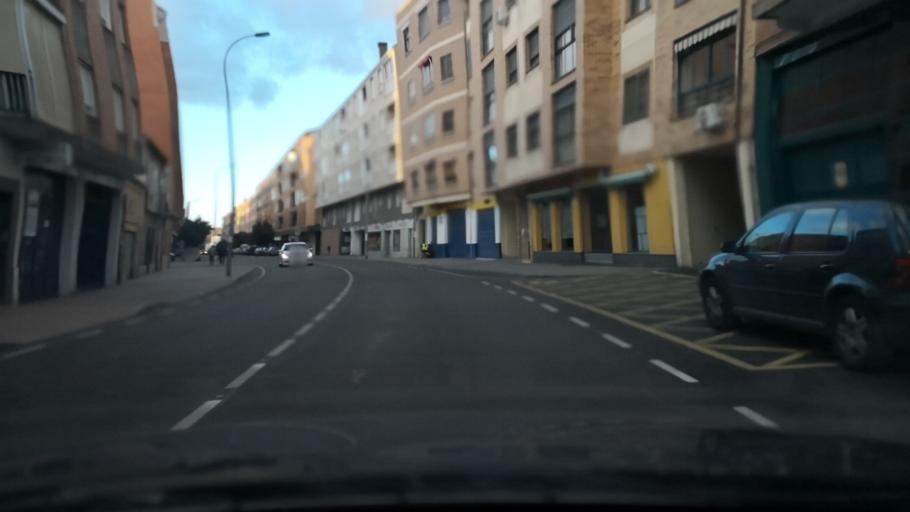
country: ES
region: Castille and Leon
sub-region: Provincia de Valladolid
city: Medina del Campo
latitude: 41.3060
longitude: -4.9109
